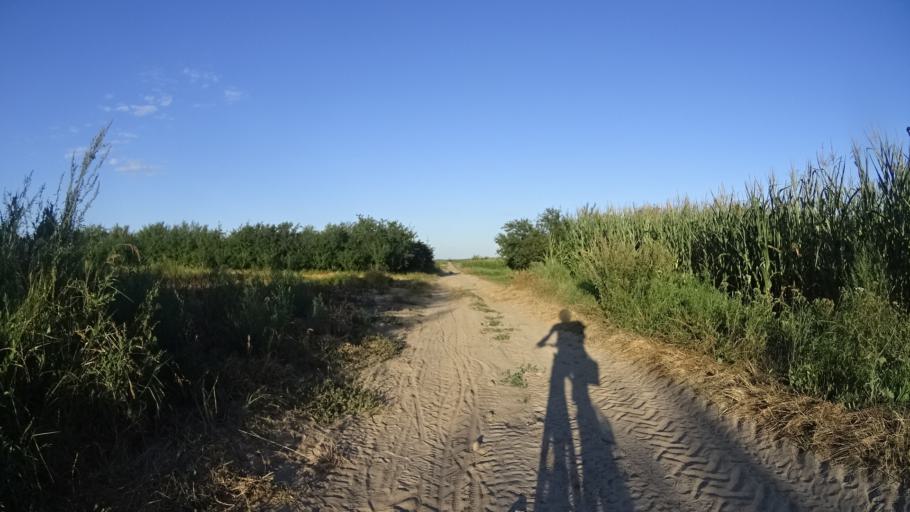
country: PL
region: Masovian Voivodeship
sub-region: Powiat bialobrzeski
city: Wysmierzyce
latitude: 51.6583
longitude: 20.7863
